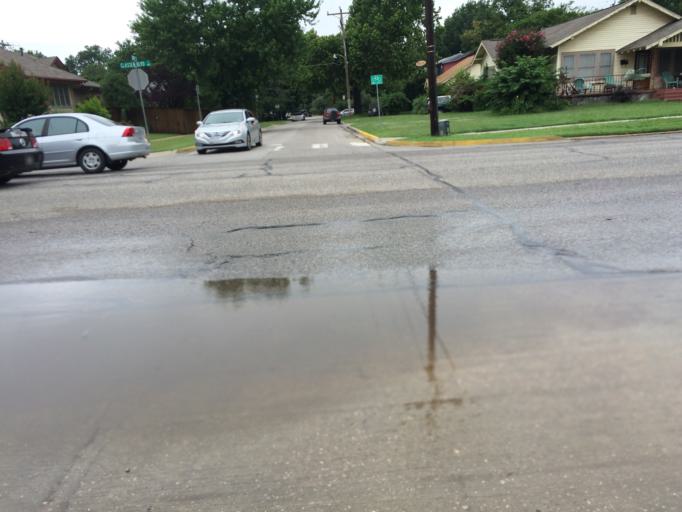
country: US
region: Oklahoma
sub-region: Cleveland County
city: Norman
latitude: 35.2154
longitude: -97.4363
